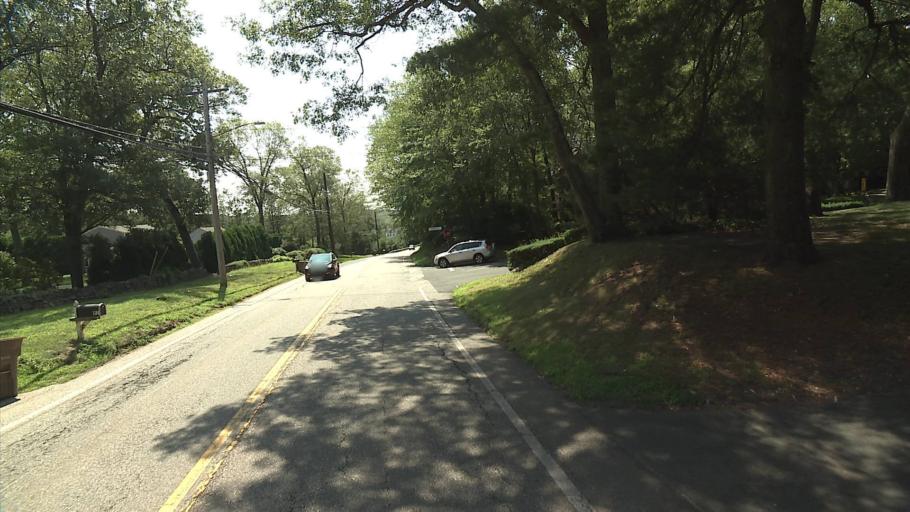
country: US
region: Connecticut
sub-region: New London County
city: Niantic
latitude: 41.3761
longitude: -72.2128
